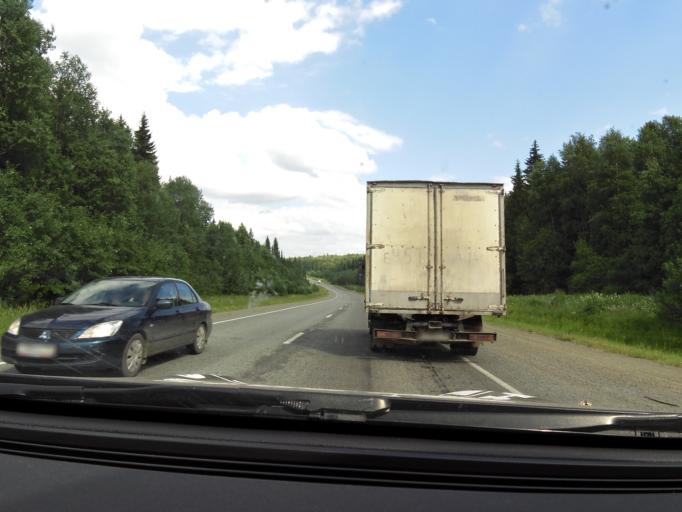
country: RU
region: Sverdlovsk
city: Bisert'
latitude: 56.8281
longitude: 59.1023
